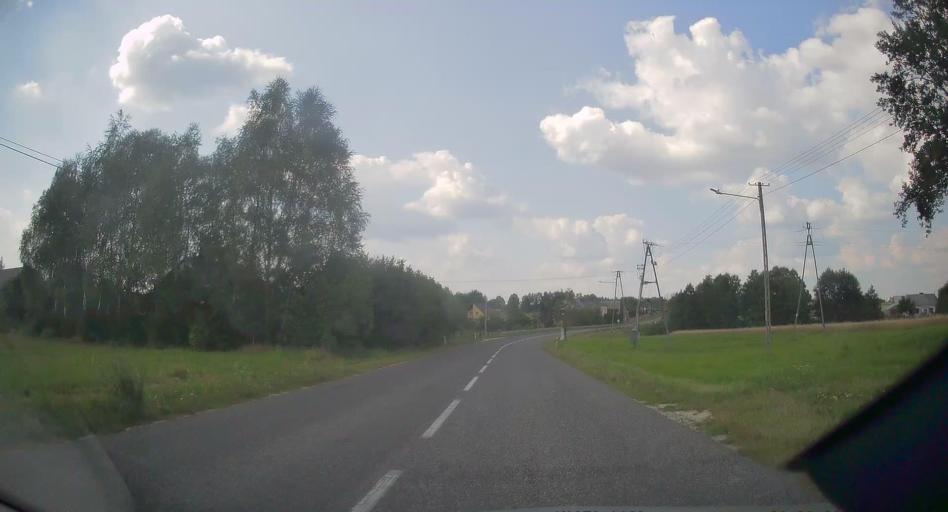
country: PL
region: Swietokrzyskie
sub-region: Powiat kielecki
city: Lopuszno
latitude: 50.9086
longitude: 20.2457
